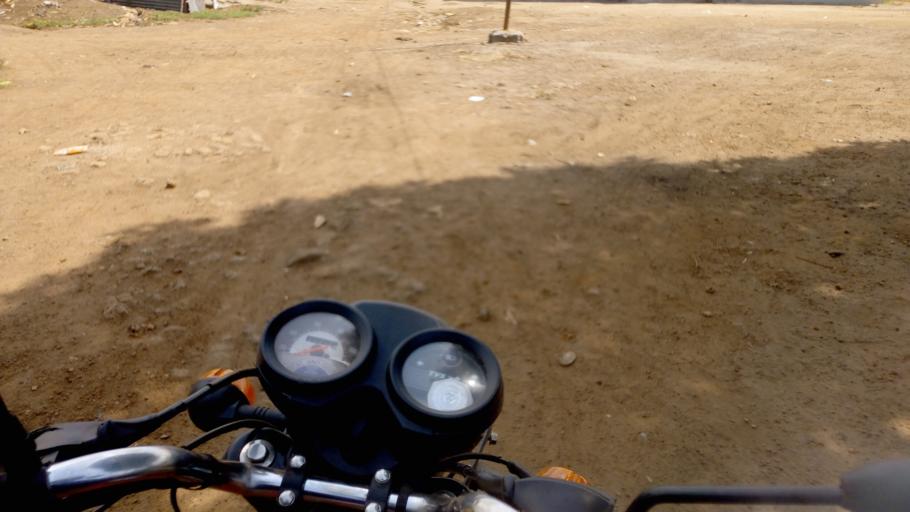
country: SL
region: Western Area
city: Waterloo
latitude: 8.3253
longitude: -13.0807
